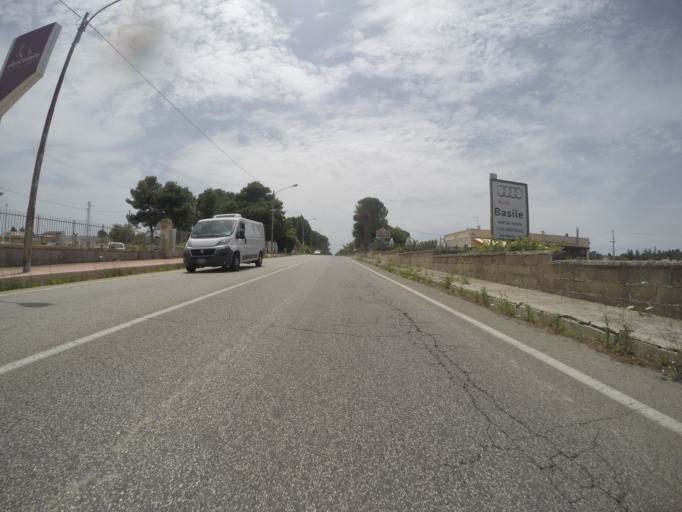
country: IT
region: Apulia
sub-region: Provincia di Taranto
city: Martina Franca
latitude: 40.6823
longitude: 17.3311
